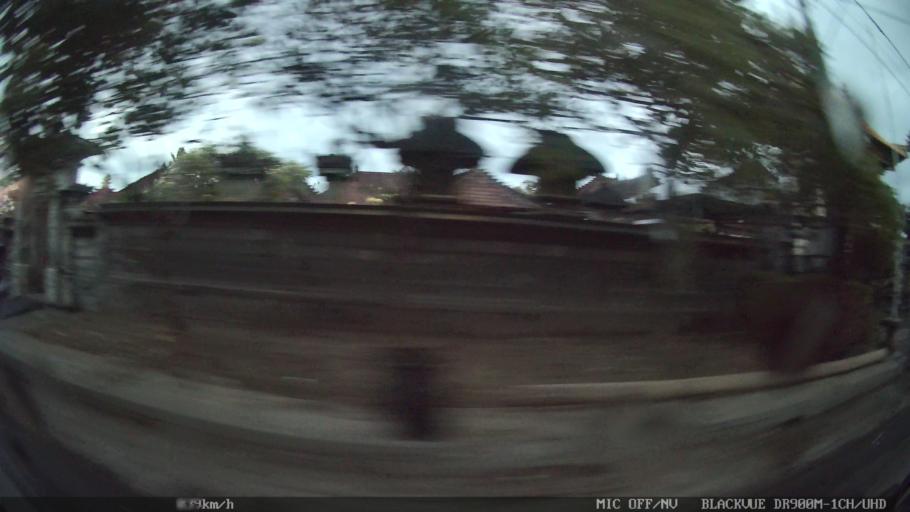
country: ID
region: Bali
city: Banjar Pasekan
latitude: -8.6229
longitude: 115.2732
